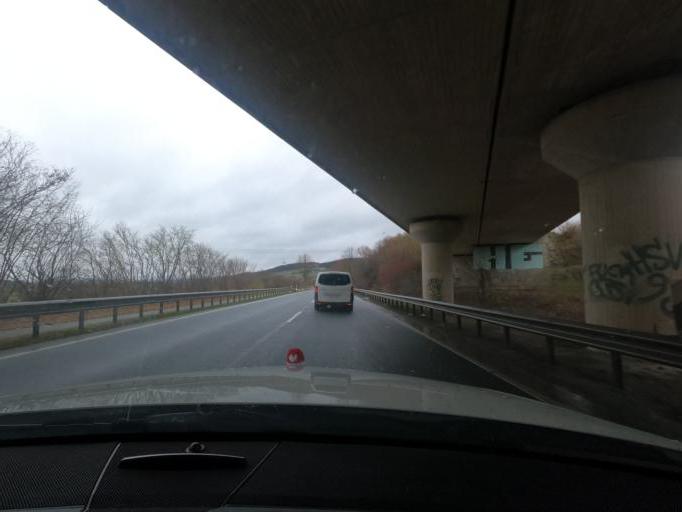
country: DE
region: Lower Saxony
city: Northeim
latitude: 51.7555
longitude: 9.9649
